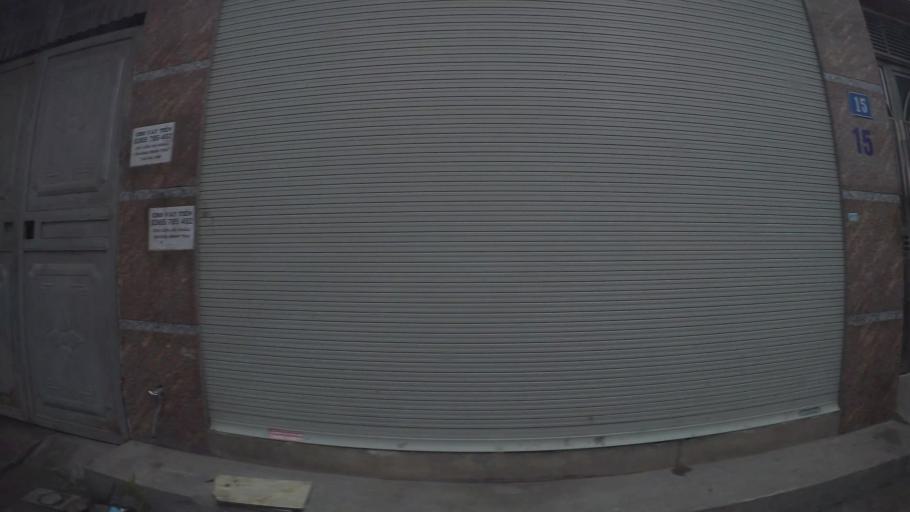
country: VN
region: Ha Noi
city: Van Dien
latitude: 20.9733
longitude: 105.8676
